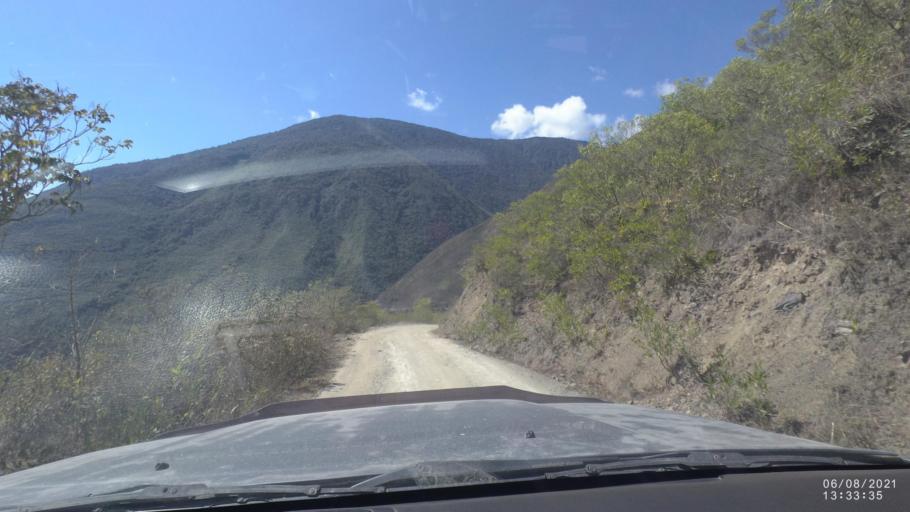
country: BO
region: La Paz
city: Quime
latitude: -16.6971
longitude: -66.7262
